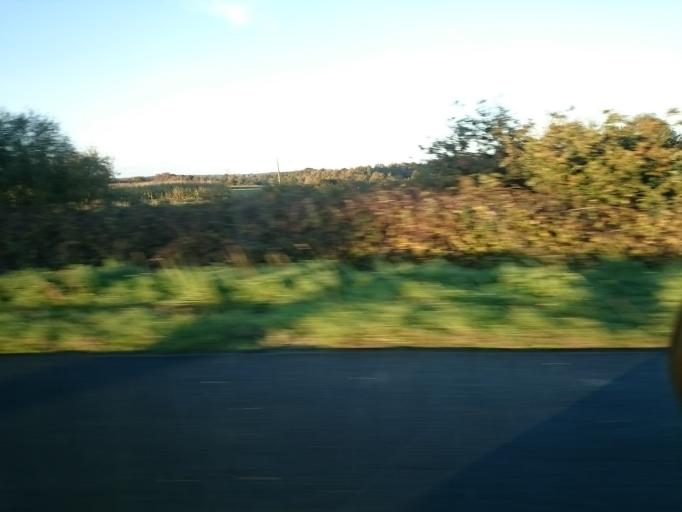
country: FR
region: Brittany
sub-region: Departement du Finistere
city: Plouigneau
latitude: 48.5787
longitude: -3.7370
